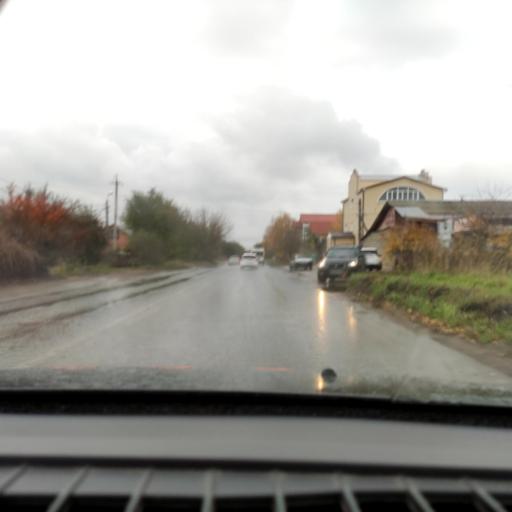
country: RU
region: Samara
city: Tol'yatti
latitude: 53.5387
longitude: 49.4199
